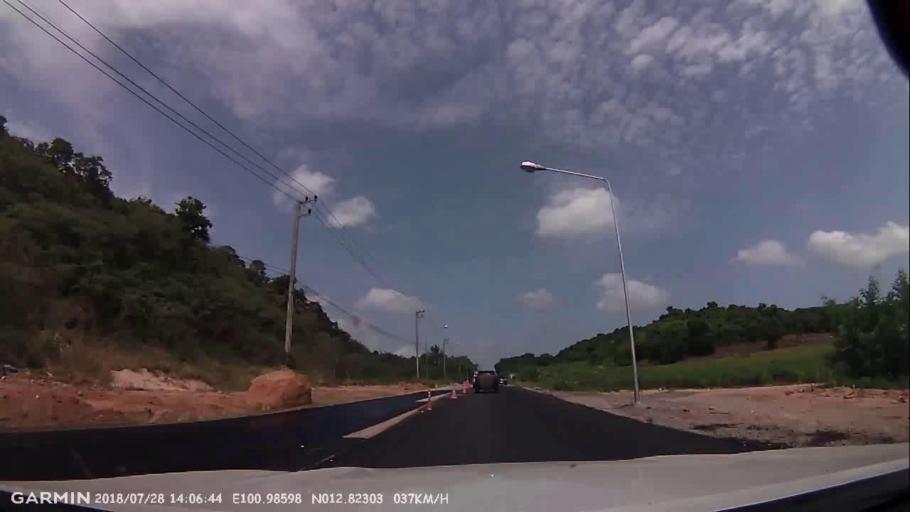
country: TH
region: Rayong
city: Ban Chang
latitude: 12.8229
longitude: 100.9861
